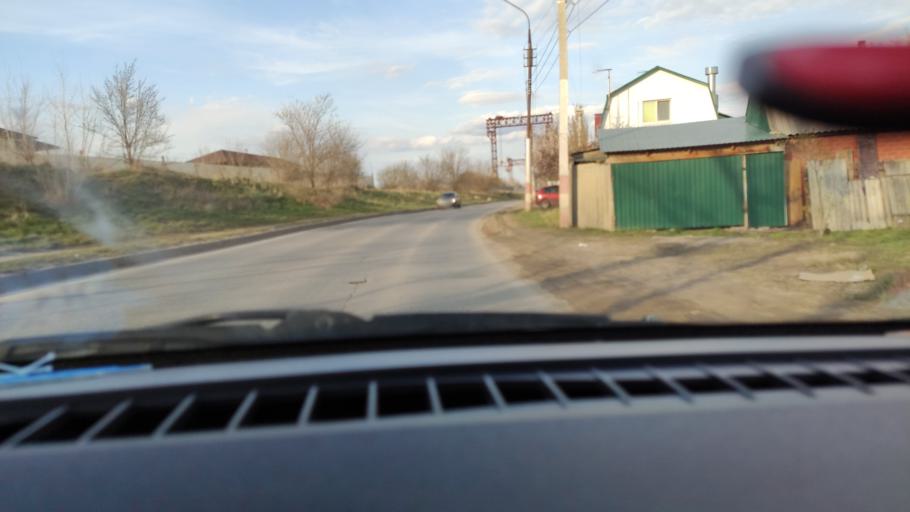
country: RU
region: Saratov
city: Engel's
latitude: 51.5035
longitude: 46.0720
